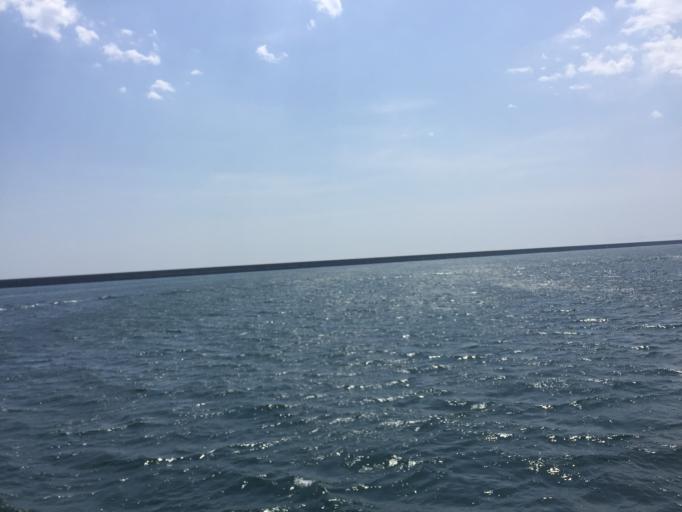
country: JP
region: Fukushima
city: Iwaki
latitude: 36.9184
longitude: 140.8972
